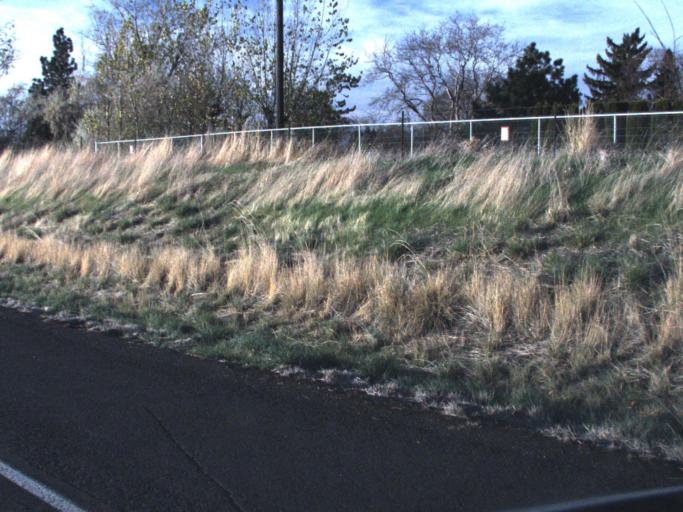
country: US
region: Washington
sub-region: Walla Walla County
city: Walla Walla East
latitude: 46.0824
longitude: -118.3133
